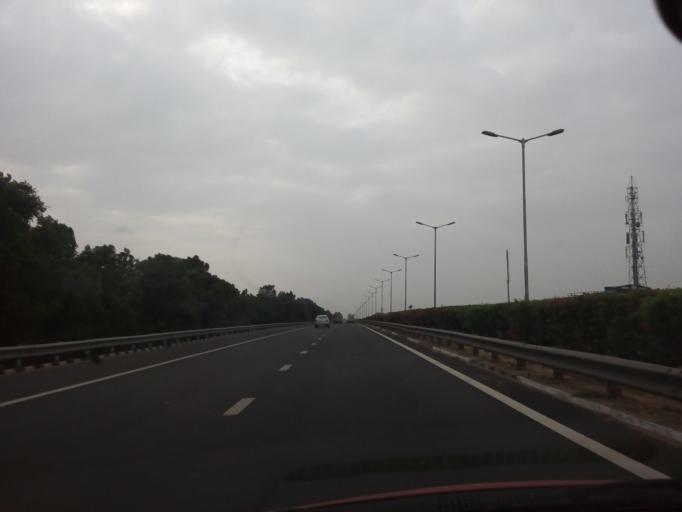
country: IN
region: Gujarat
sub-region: Ahmadabad
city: Ahmedabad
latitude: 22.9810
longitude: 72.6414
